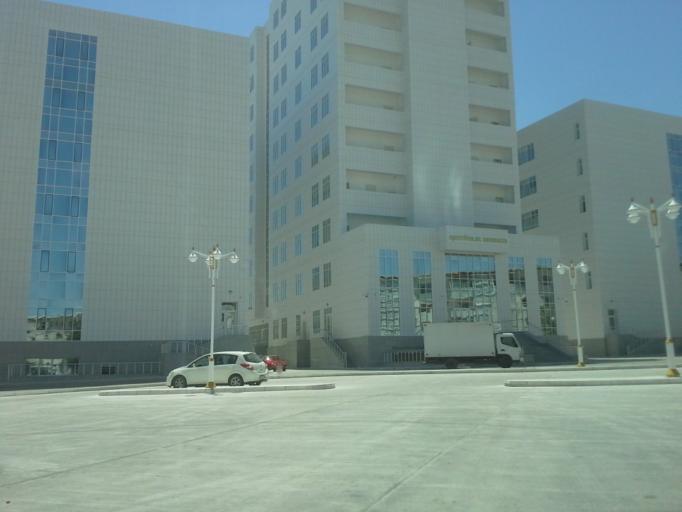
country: TM
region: Ahal
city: Ashgabat
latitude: 37.9118
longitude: 58.3967
